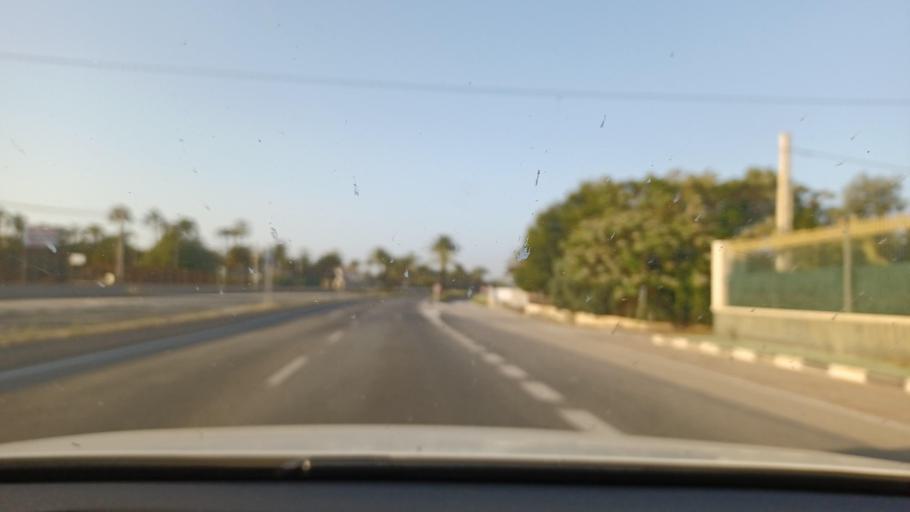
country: ES
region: Valencia
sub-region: Provincia de Alicante
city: Elche
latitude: 38.2477
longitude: -0.6981
